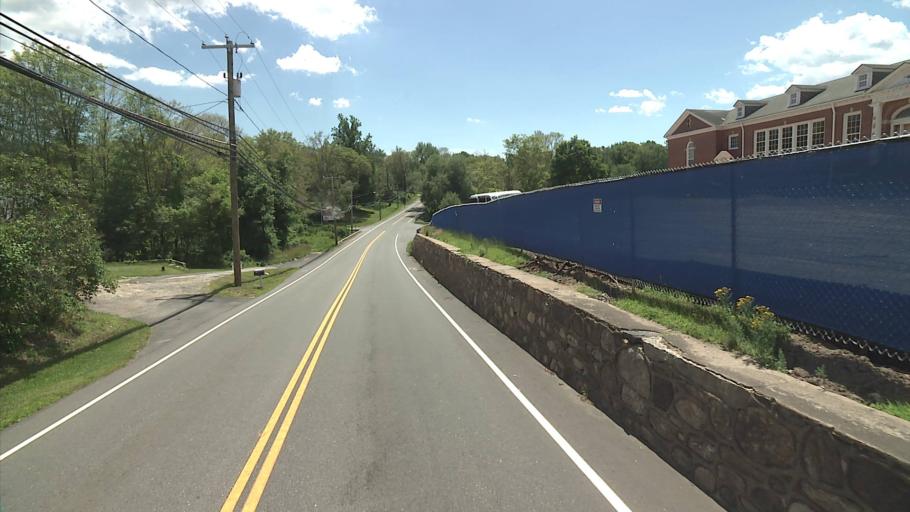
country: US
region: Connecticut
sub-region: Middlesex County
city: Moodus
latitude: 41.4990
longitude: -72.4493
